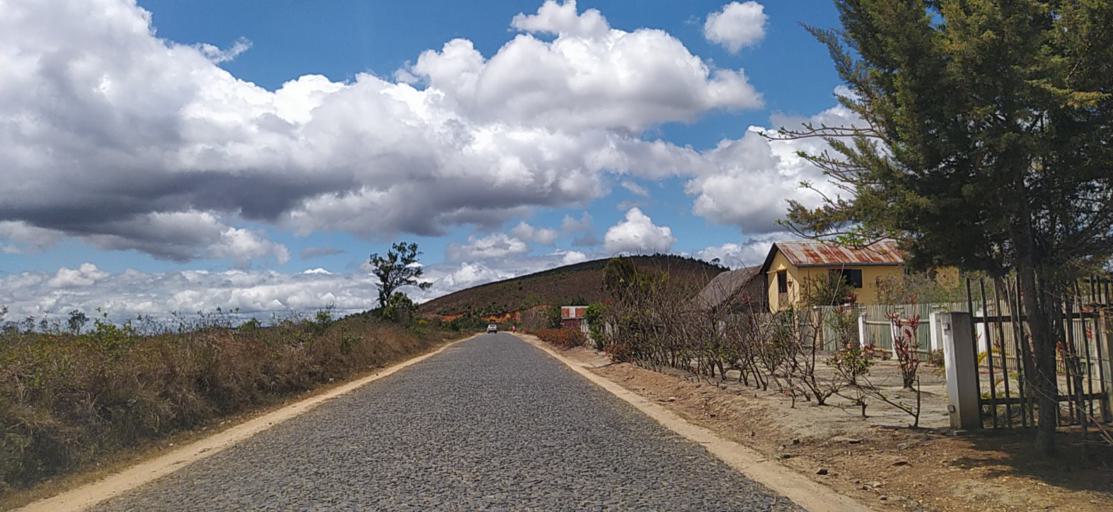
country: MG
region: Alaotra Mangoro
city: Moramanga
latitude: -18.7603
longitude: 48.2571
